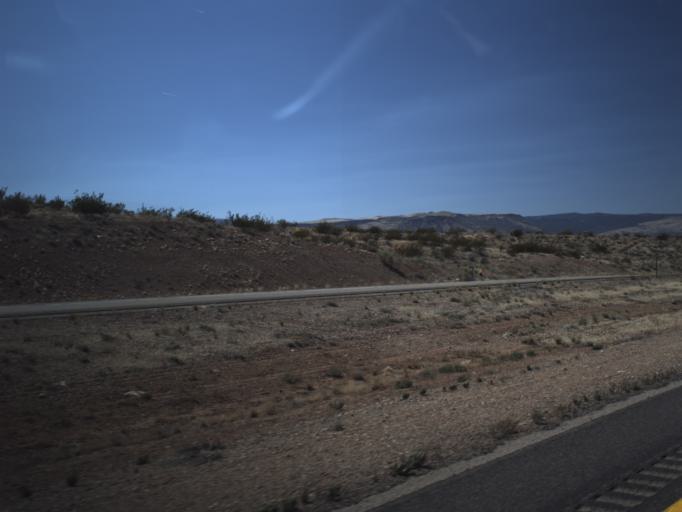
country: US
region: Utah
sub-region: Washington County
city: Saint George
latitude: 37.0066
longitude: -113.5208
